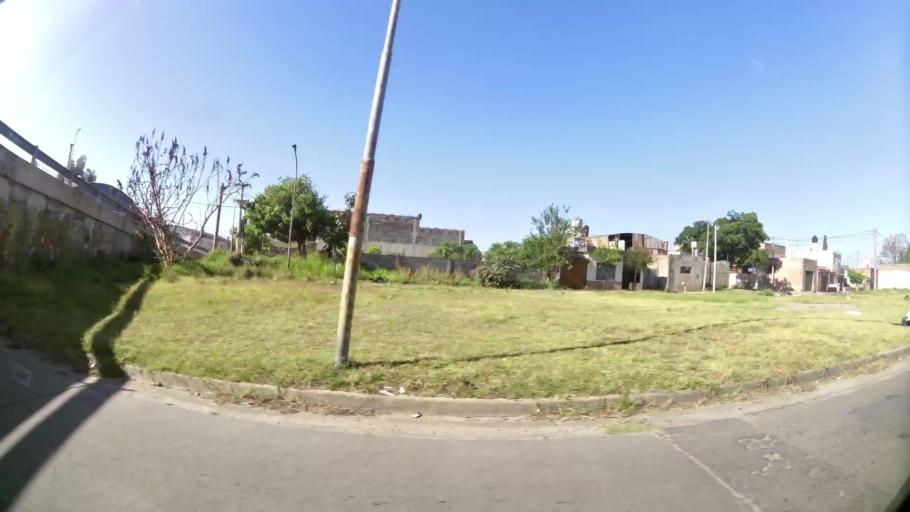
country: AR
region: Cordoba
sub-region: Departamento de Capital
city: Cordoba
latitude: -31.4185
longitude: -64.1514
